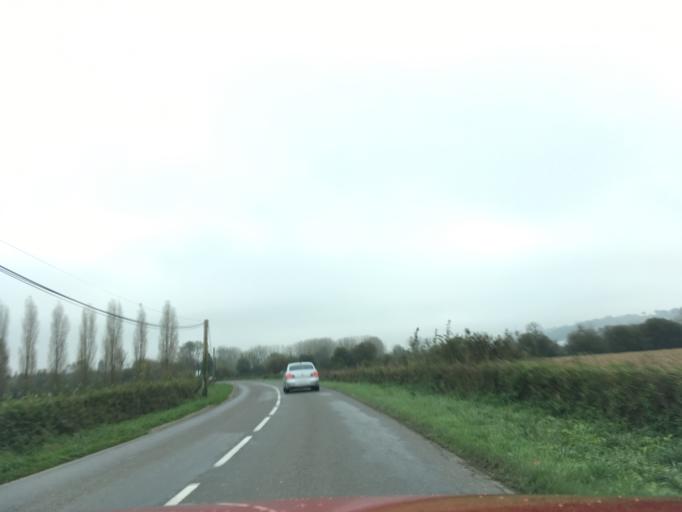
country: FR
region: Lower Normandy
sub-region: Departement de la Manche
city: Avranches
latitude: 48.6948
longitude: -1.3687
